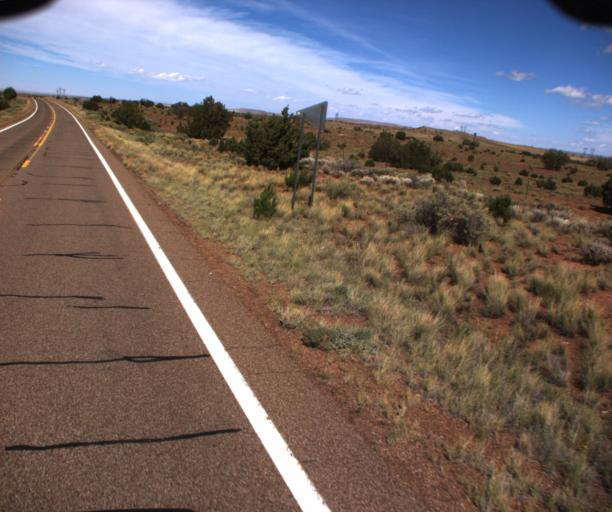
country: US
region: Arizona
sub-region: Apache County
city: Saint Johns
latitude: 34.5317
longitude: -109.6202
